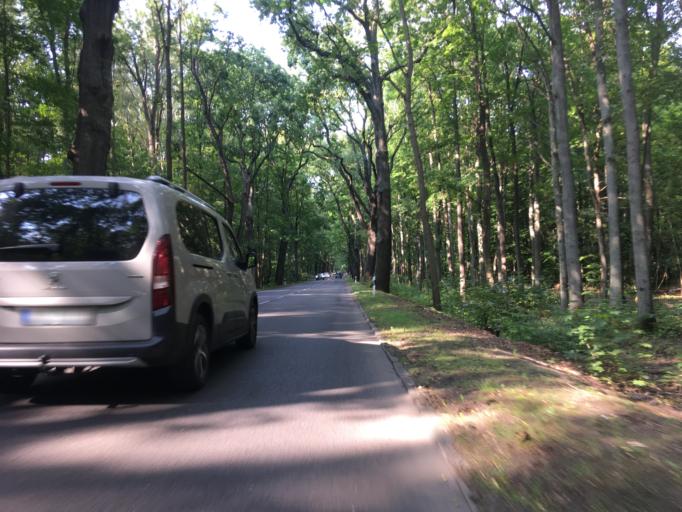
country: DE
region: Berlin
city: Frohnau
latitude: 52.6518
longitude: 13.2936
